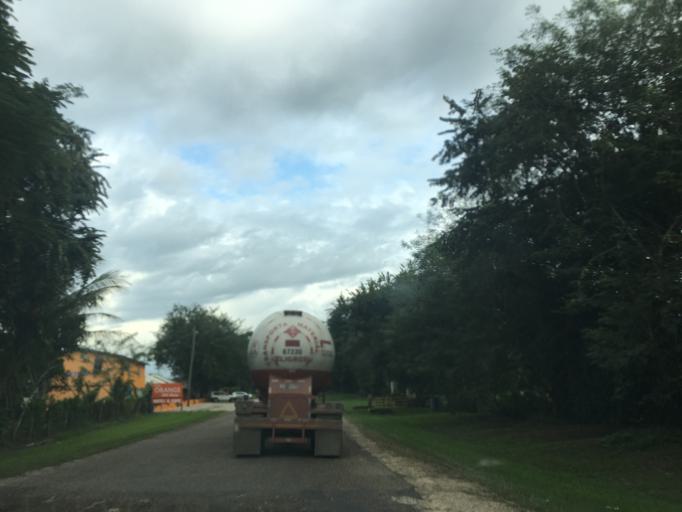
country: BZ
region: Cayo
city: San Ignacio
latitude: 17.2035
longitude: -88.9545
